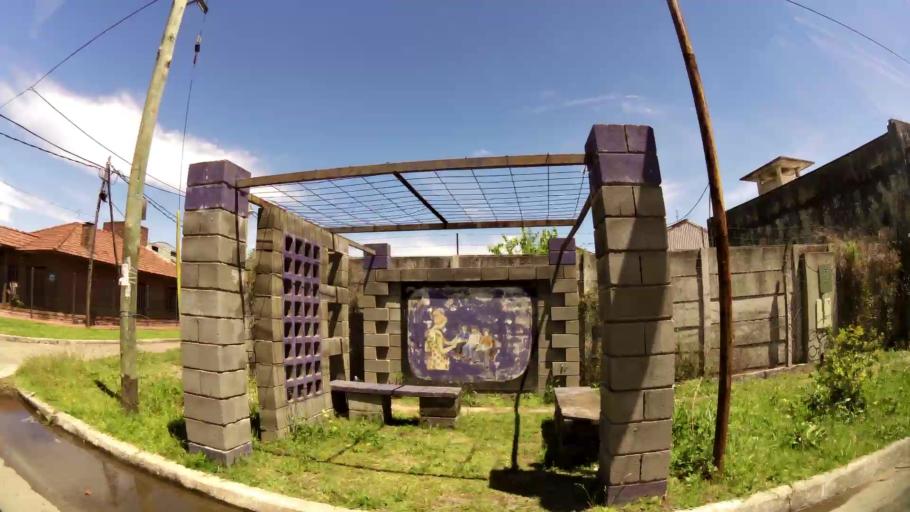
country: AR
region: Buenos Aires
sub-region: Partido de Quilmes
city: Quilmes
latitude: -34.7479
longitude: -58.2841
